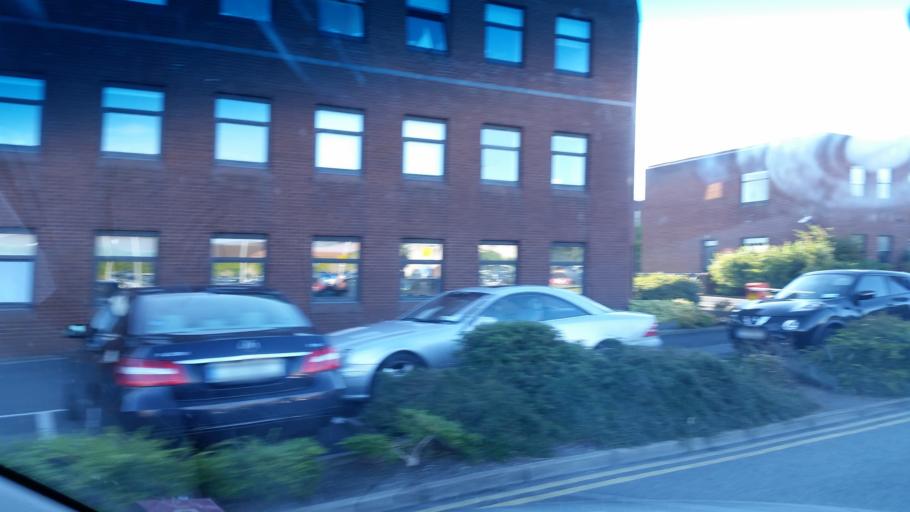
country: IE
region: Leinster
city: Artane
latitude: 53.3914
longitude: -6.2253
